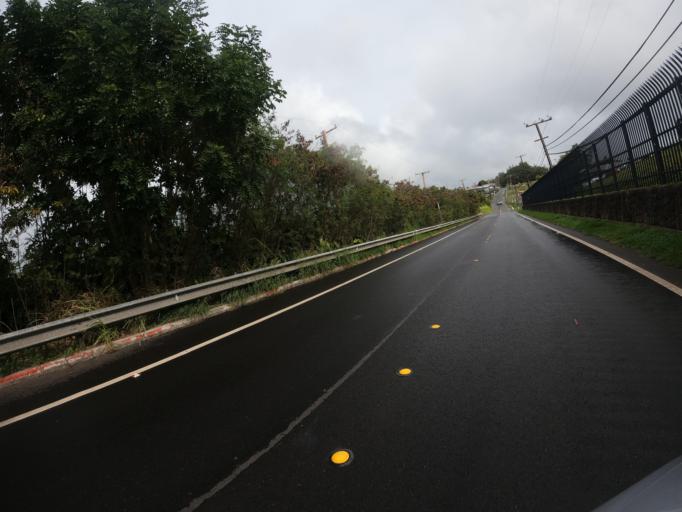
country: US
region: Hawaii
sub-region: Honolulu County
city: Halawa Heights
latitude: 21.3870
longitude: -157.9078
